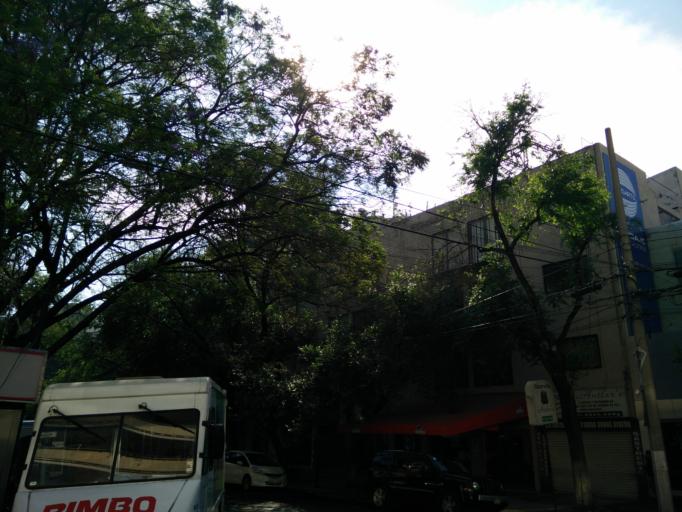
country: MX
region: Mexico City
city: Miguel Hidalgo
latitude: 19.4323
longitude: -99.1903
